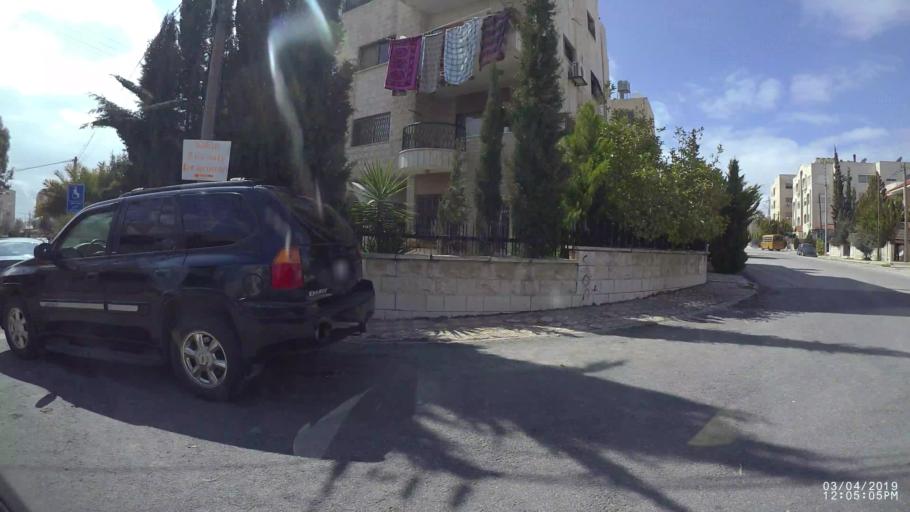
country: JO
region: Amman
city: Wadi as Sir
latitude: 31.9616
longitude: 35.8419
